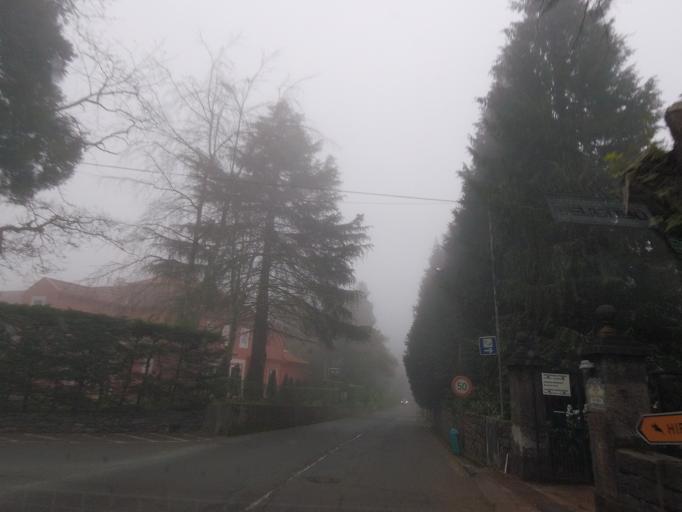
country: PT
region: Madeira
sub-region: Santa Cruz
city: Santa Cruz
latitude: 32.7239
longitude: -16.8178
